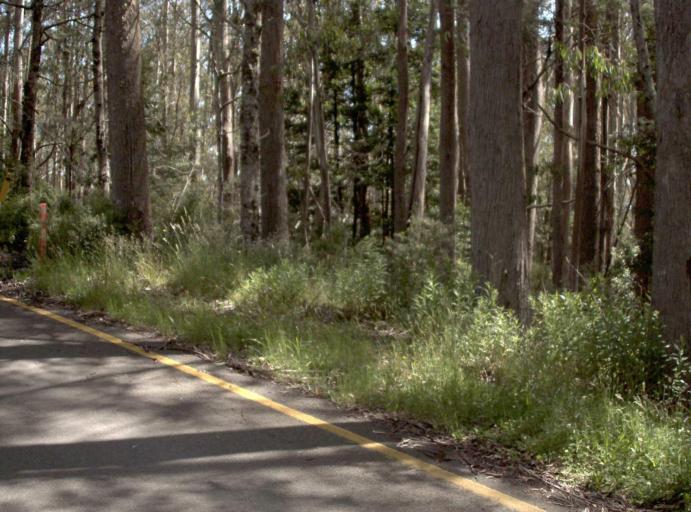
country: AU
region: Victoria
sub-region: Latrobe
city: Moe
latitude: -37.8456
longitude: 146.2551
